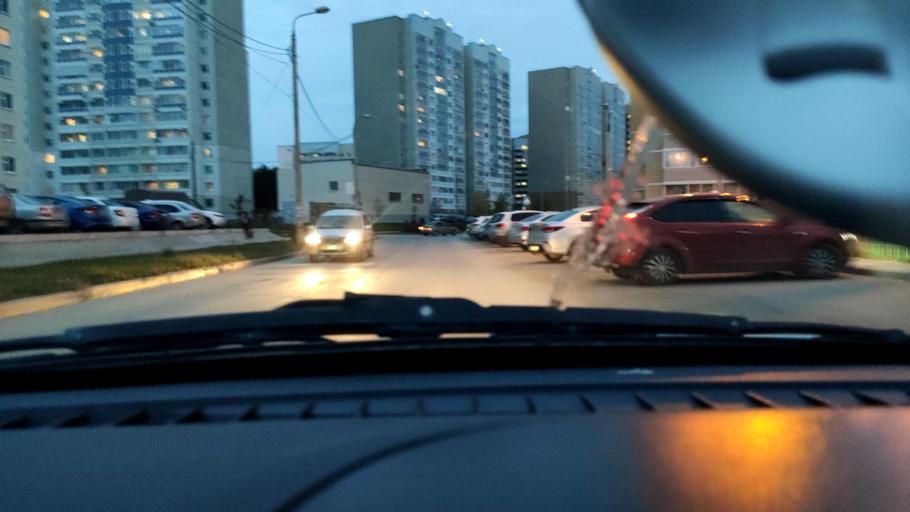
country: RU
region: Perm
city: Kondratovo
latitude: 58.0332
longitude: 56.1400
